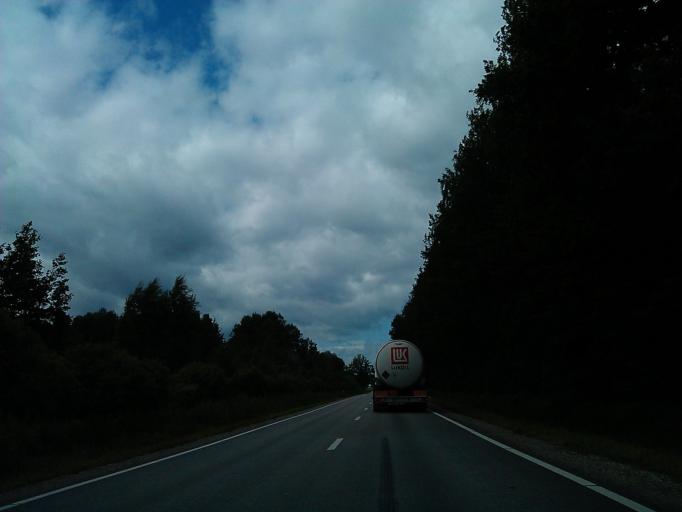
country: LV
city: Tireli
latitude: 56.9272
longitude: 23.5572
